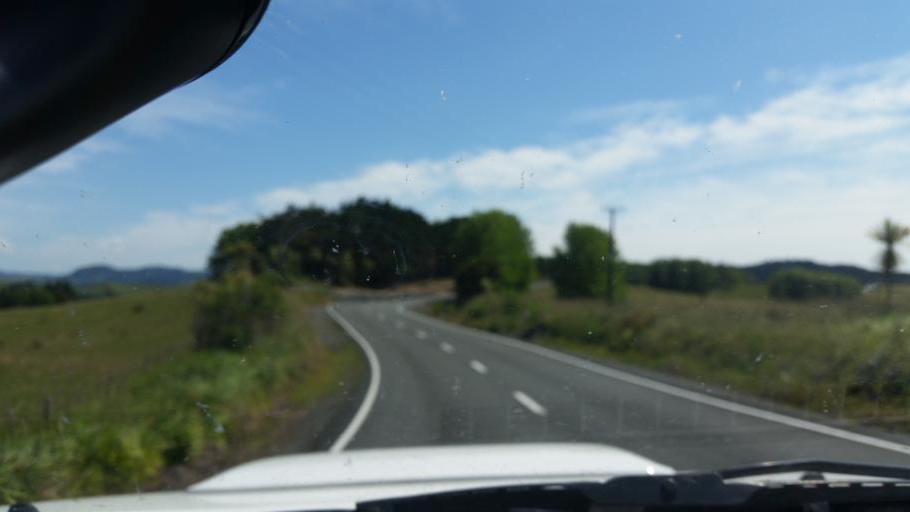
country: NZ
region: Auckland
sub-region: Auckland
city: Wellsford
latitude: -36.2217
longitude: 174.3797
